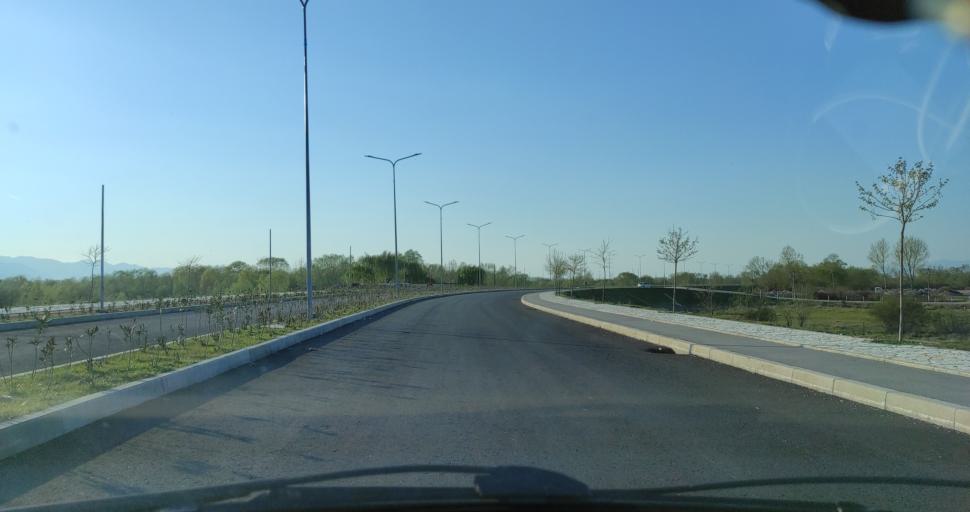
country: AL
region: Shkoder
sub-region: Rrethi i Shkodres
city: Shkoder
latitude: 42.0643
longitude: 19.4911
